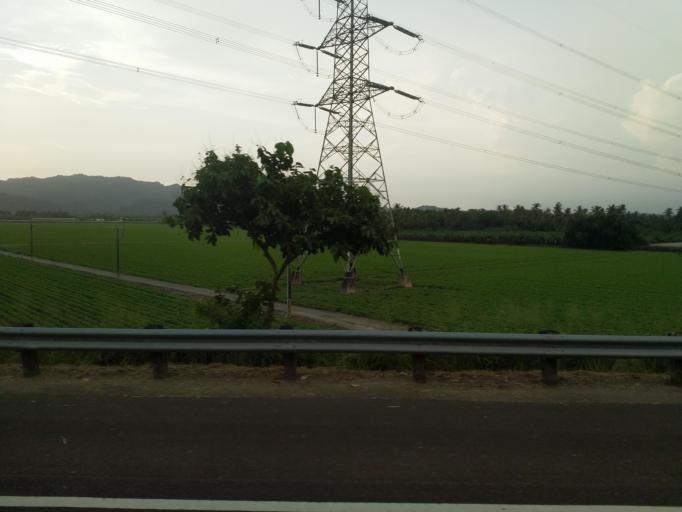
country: TW
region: Taiwan
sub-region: Pingtung
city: Pingtung
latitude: 22.8319
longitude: 120.4915
